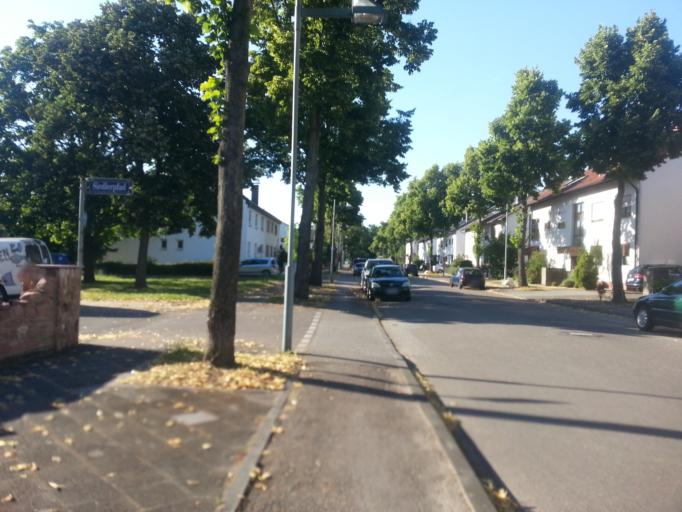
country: DE
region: Baden-Wuerttemberg
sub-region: Karlsruhe Region
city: Mannheim
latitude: 49.5279
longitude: 8.5103
